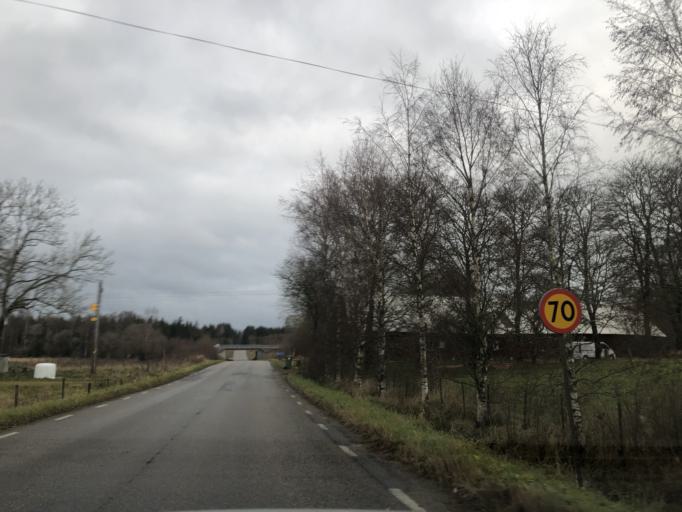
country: SE
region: Vaestra Goetaland
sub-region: Boras Kommun
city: Dalsjofors
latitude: 57.8066
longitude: 13.1977
